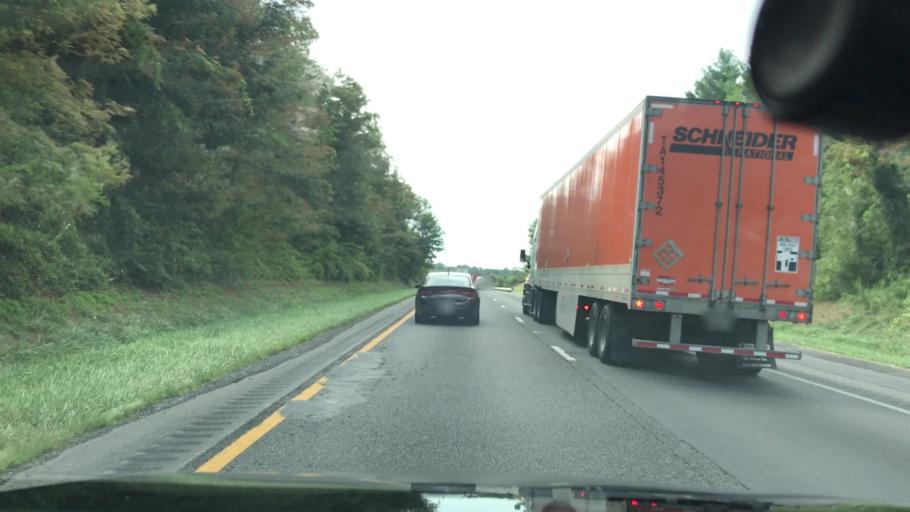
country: US
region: Virginia
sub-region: Carroll County
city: Woodlawn
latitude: 36.7624
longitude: -80.7952
